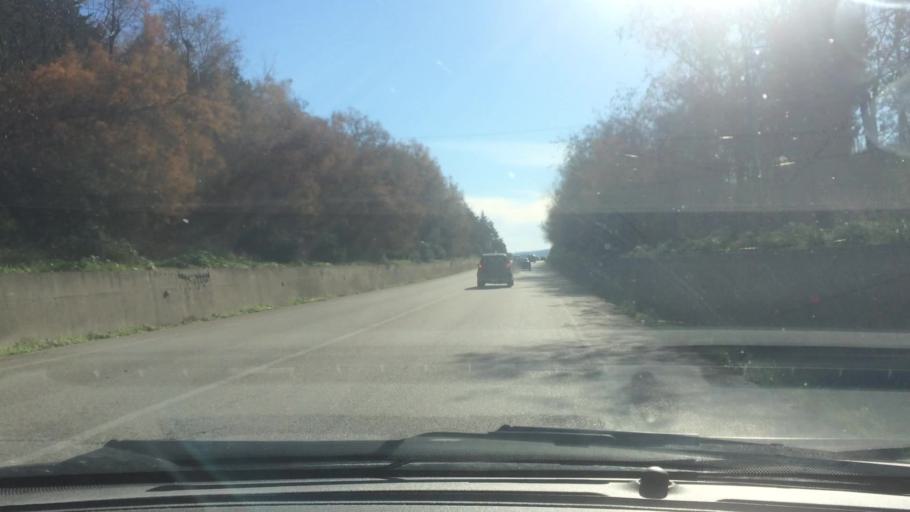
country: IT
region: Basilicate
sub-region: Provincia di Matera
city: Pomarico
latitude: 40.5900
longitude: 16.5745
